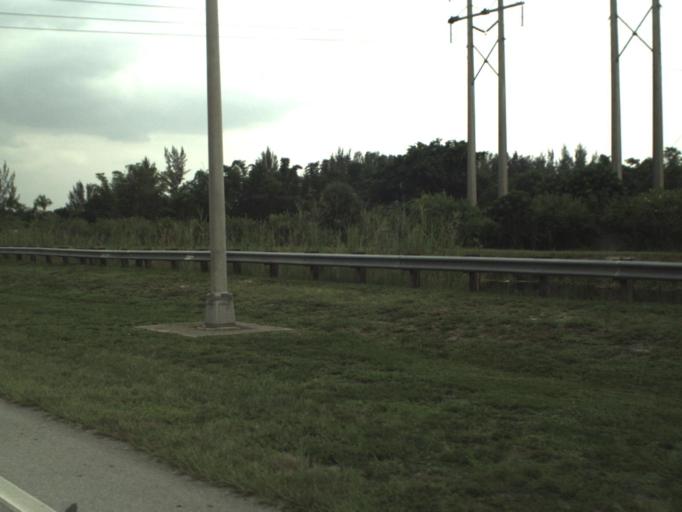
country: US
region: Florida
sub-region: Broward County
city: Sunshine Ranches
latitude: 26.0361
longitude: -80.3129
